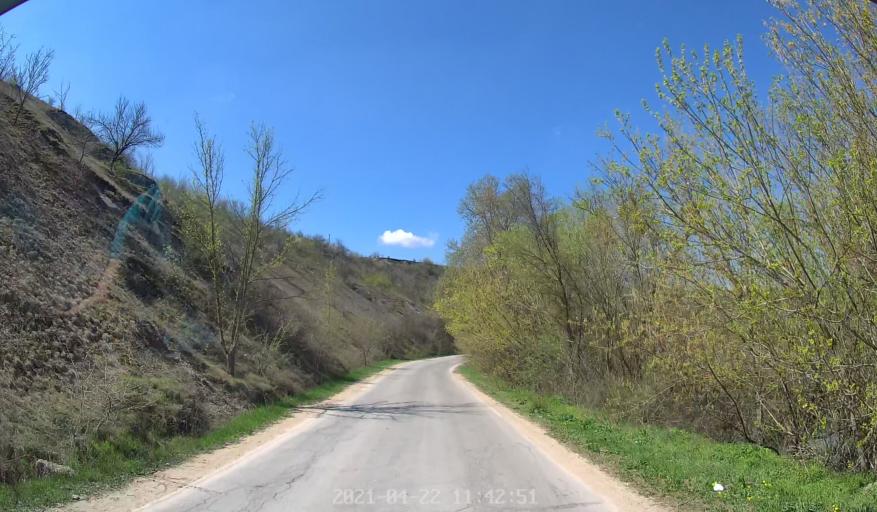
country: MD
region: Chisinau
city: Ciorescu
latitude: 47.1369
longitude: 28.9047
